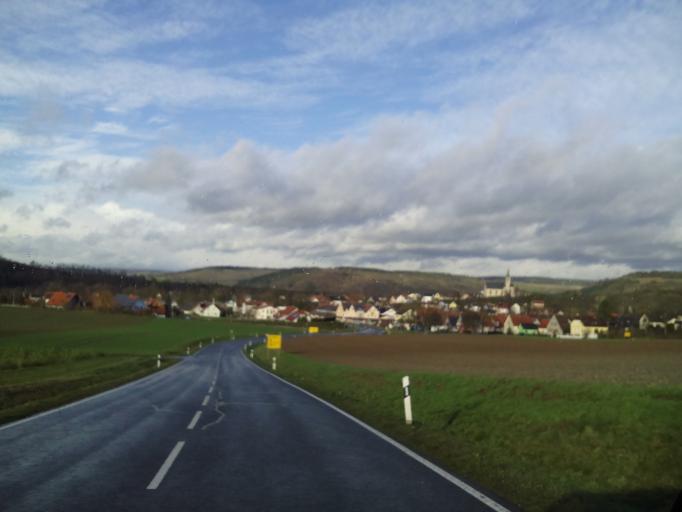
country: DE
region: Bavaria
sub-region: Regierungsbezirk Unterfranken
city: Eussenheim
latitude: 49.9815
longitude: 9.8088
